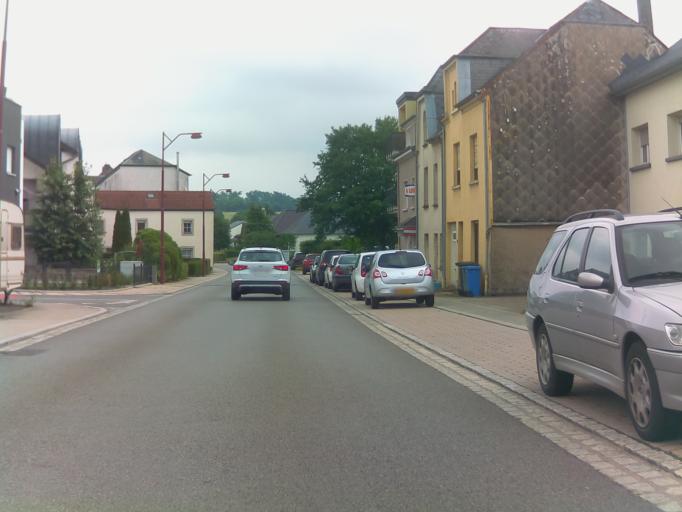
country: LU
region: Luxembourg
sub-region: Canton de Capellen
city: Steinfort
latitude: 49.6487
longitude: 5.9318
